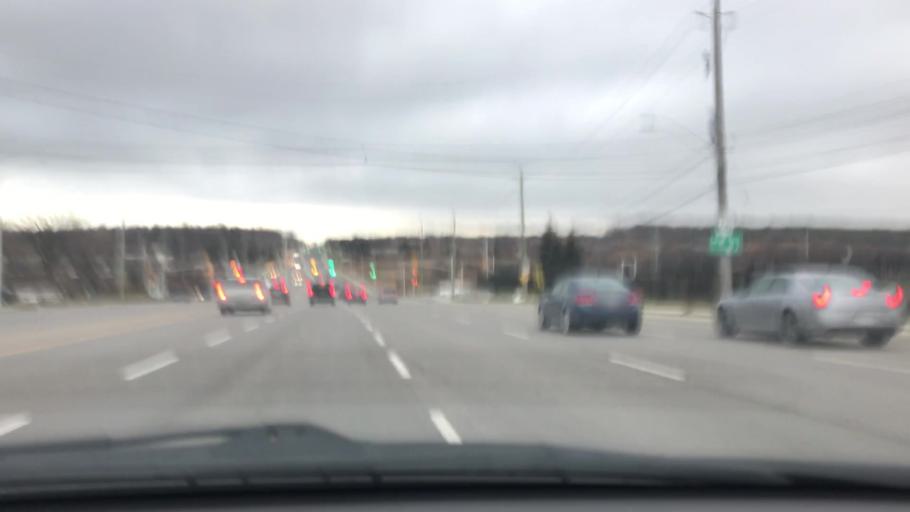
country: CA
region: Ontario
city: Oakville
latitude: 43.4966
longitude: -79.6784
